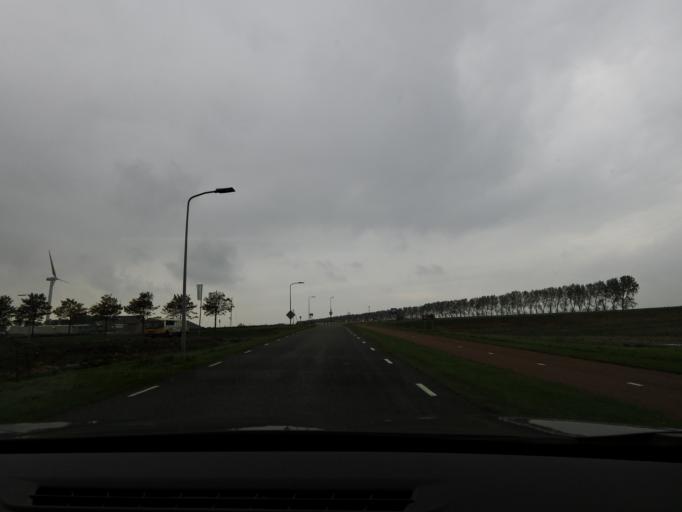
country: NL
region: South Holland
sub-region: Gemeente Goeree-Overflakkee
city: Middelharnis
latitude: 51.7689
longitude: 4.1841
